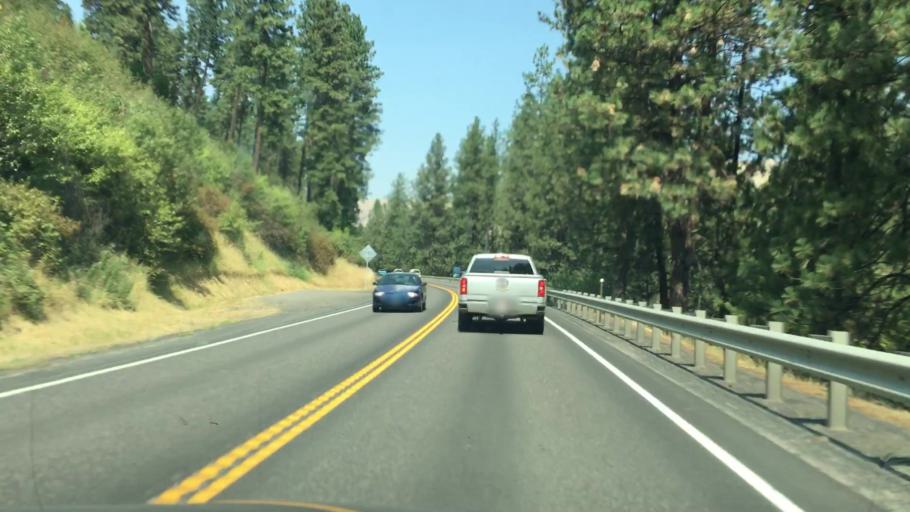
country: US
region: Idaho
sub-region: Nez Perce County
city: Lapwai
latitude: 46.5118
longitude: -116.5817
